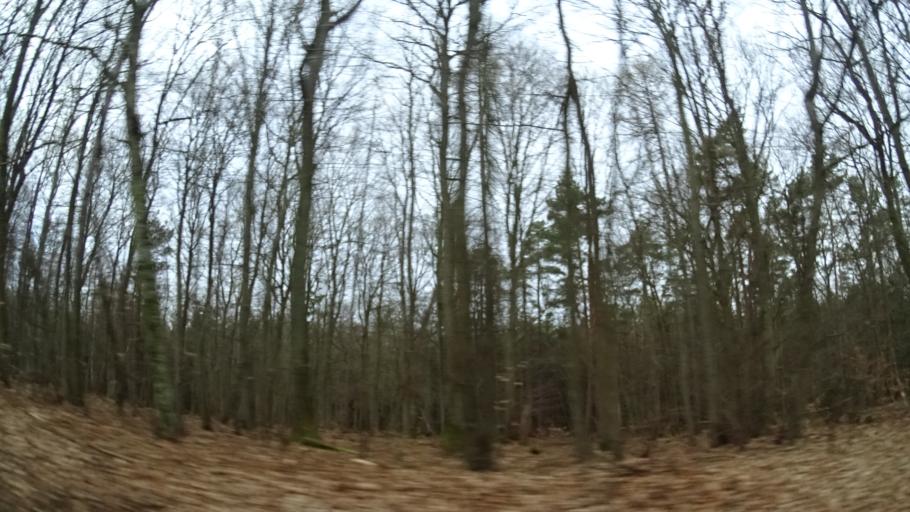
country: DE
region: Rheinland-Pfalz
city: Daubach
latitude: 49.8328
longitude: 7.6357
